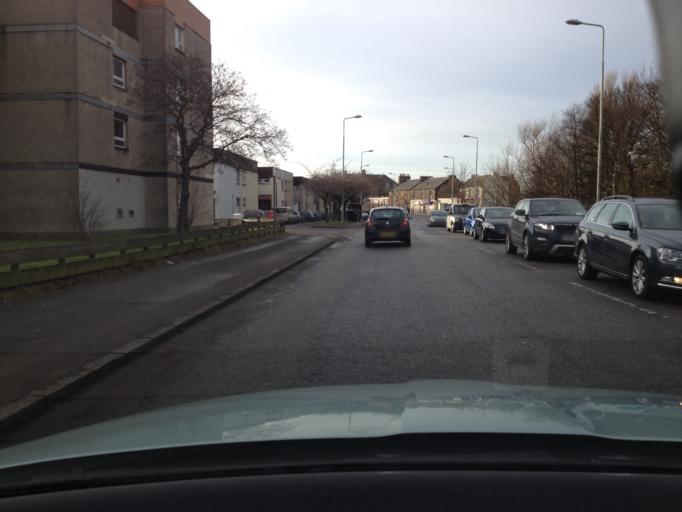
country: GB
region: Scotland
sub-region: Edinburgh
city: Colinton
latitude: 55.9251
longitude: -3.2569
